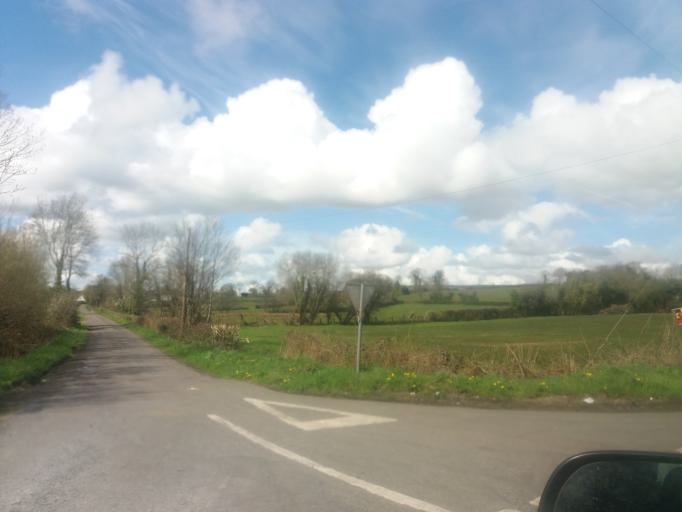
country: IE
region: Ulster
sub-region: An Cabhan
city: Belturbet
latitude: 54.1412
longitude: -7.5111
